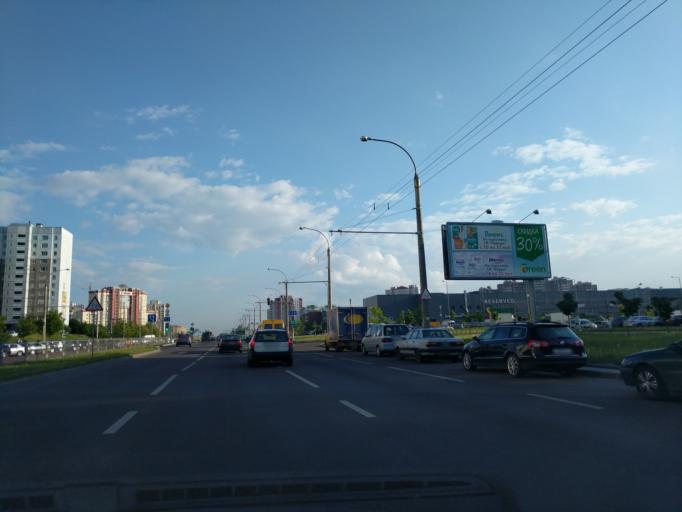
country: BY
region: Minsk
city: Novoye Medvezhino
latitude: 53.9107
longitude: 27.4361
